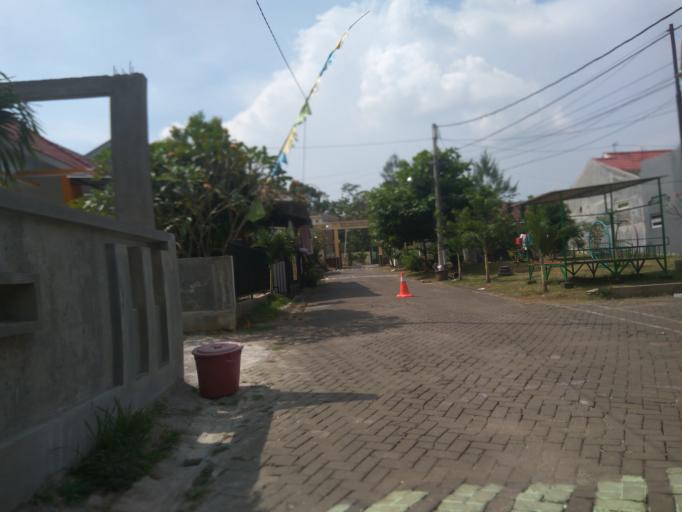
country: ID
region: Central Java
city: Ungaran
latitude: -7.0729
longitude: 110.4457
